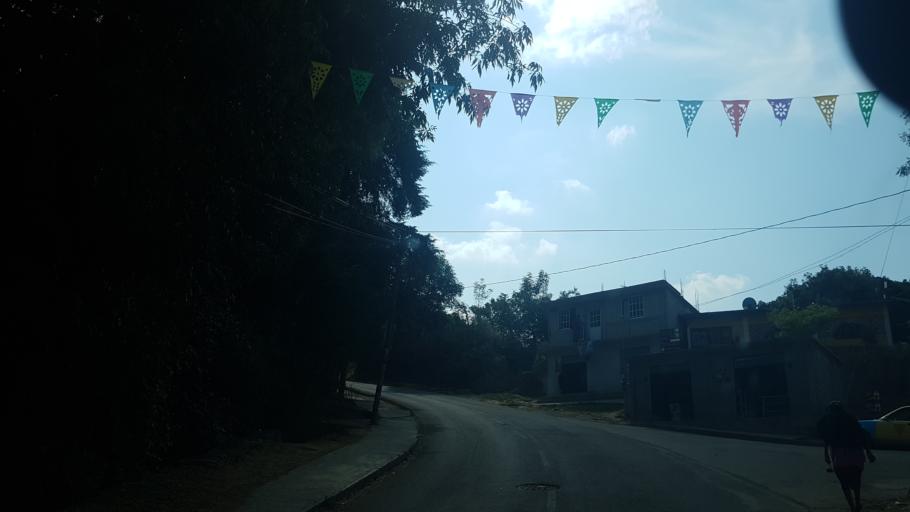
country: MX
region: Puebla
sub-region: Tochimilco
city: San Antonio Alpanocan
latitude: 18.8774
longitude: -98.7039
